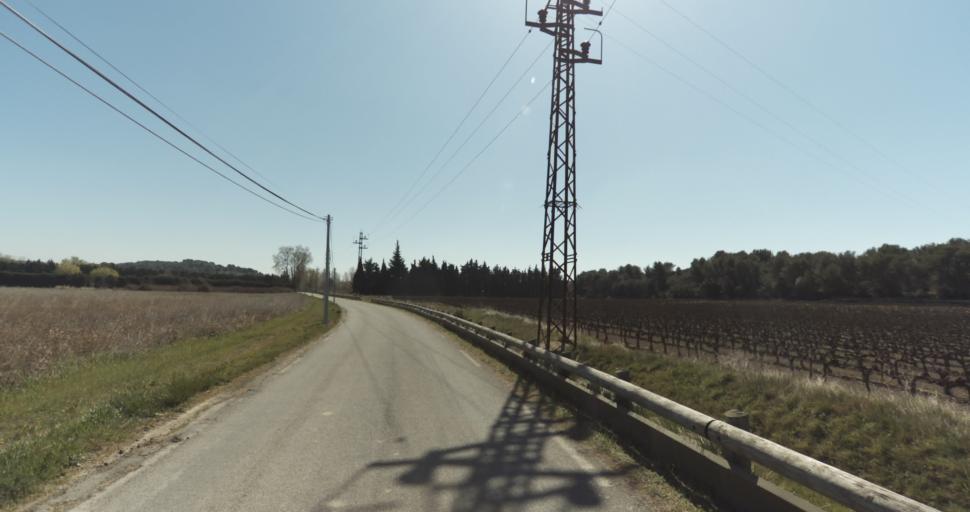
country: FR
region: Provence-Alpes-Cote d'Azur
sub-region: Departement des Bouches-du-Rhone
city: Pelissanne
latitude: 43.6187
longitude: 5.1612
